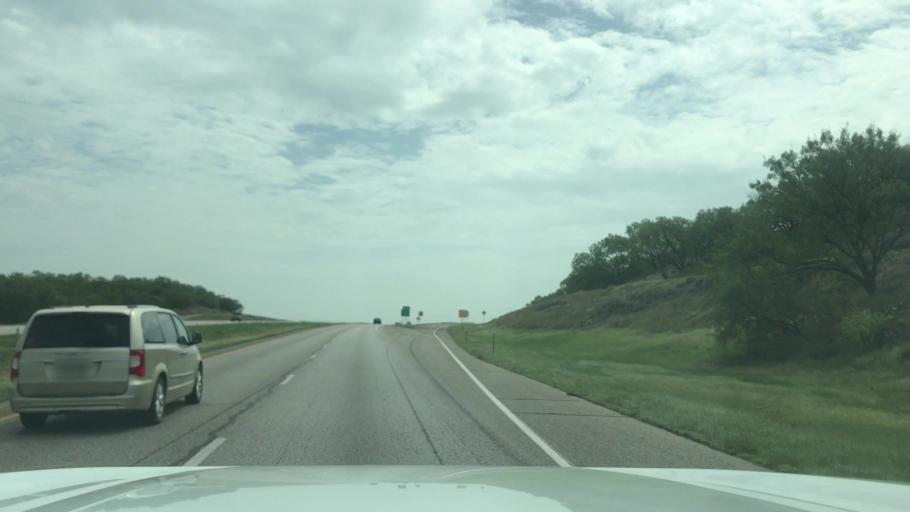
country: US
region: Texas
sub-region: Eastland County
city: Cisco
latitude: 32.3793
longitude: -99.1487
